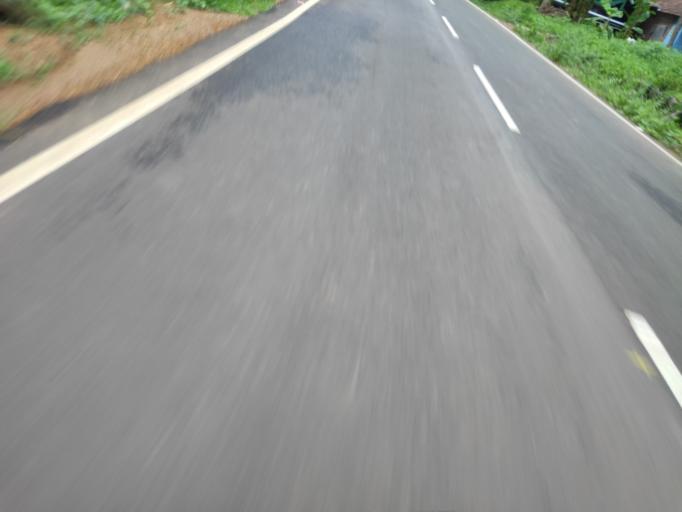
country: IN
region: Kerala
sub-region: Malappuram
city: Manjeri
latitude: 11.1865
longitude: 76.2130
